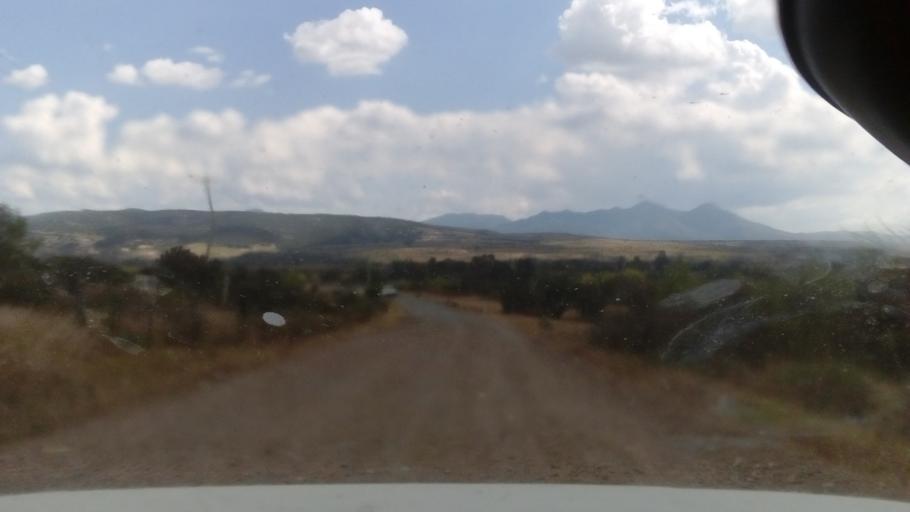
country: MX
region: Guanajuato
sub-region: Silao de la Victoria
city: San Francisco (Banos de Agua Caliente)
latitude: 21.1993
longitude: -101.4454
